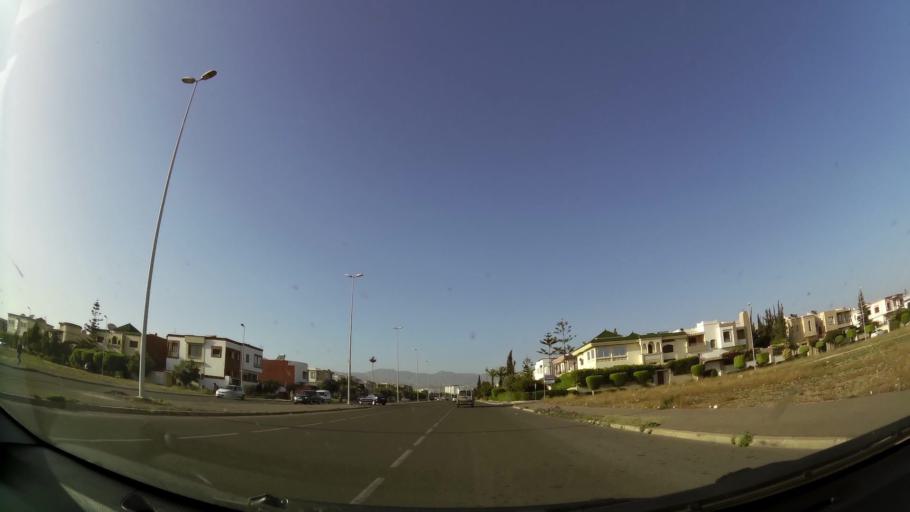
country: MA
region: Oued ed Dahab-Lagouira
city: Dakhla
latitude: 30.4008
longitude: -9.5409
